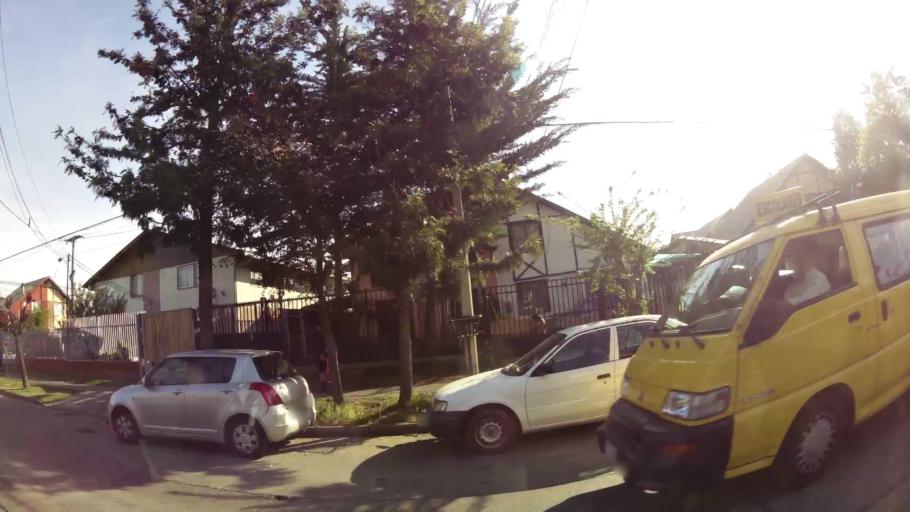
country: CL
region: Santiago Metropolitan
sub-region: Provincia de Santiago
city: Villa Presidente Frei, Nunoa, Santiago, Chile
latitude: -33.5269
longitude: -70.5804
